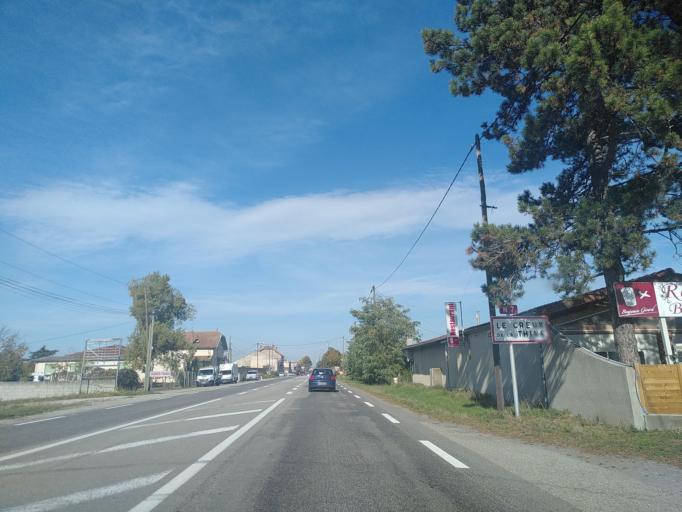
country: FR
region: Rhone-Alpes
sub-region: Departement de la Drome
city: Andancette
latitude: 45.2562
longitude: 4.8228
